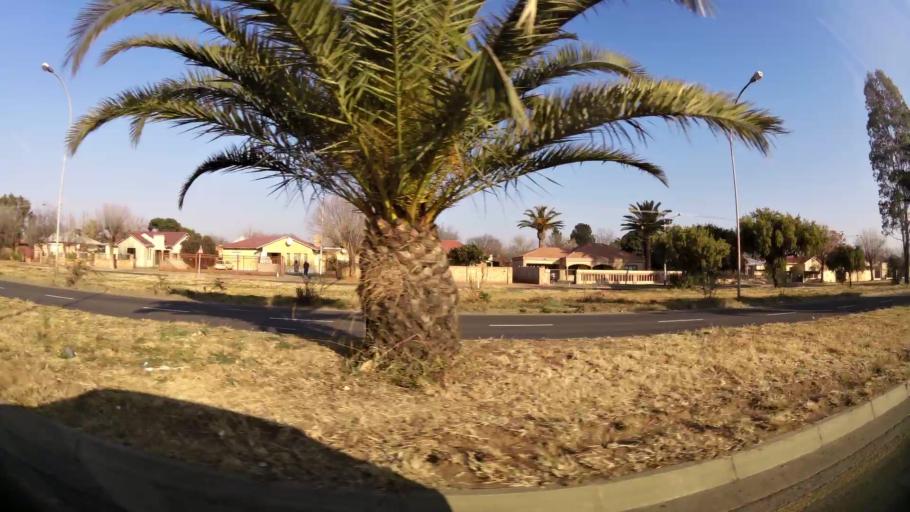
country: ZA
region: Orange Free State
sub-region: Mangaung Metropolitan Municipality
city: Bloemfontein
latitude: -29.1483
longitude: 26.2169
